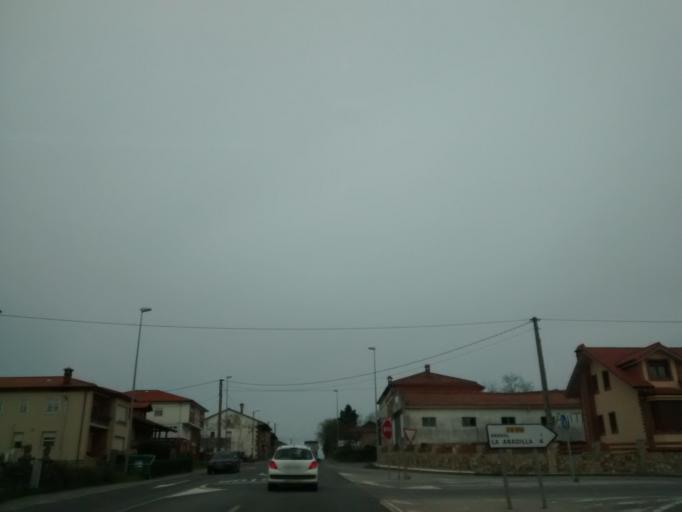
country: ES
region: Cantabria
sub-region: Provincia de Cantabria
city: Penagos
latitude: 43.3395
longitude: -3.8212
